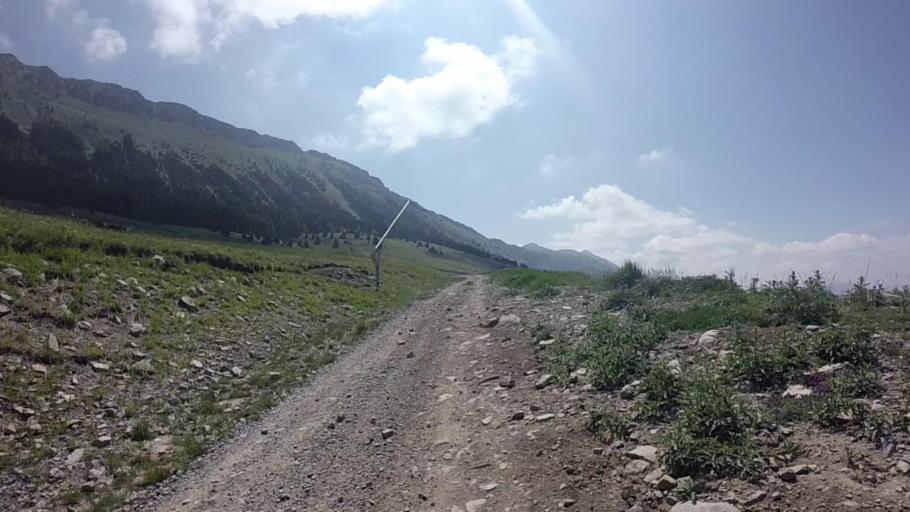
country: FR
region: Provence-Alpes-Cote d'Azur
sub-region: Departement des Alpes-de-Haute-Provence
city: Seyne-les-Alpes
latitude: 44.3990
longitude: 6.3742
